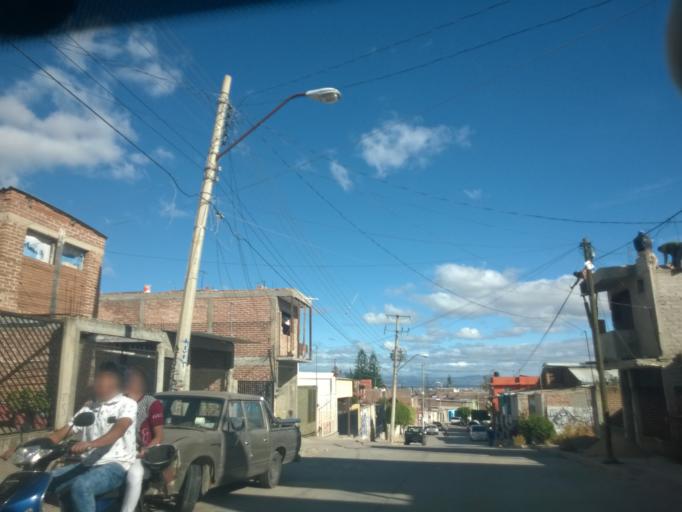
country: MX
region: Guanajuato
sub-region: Leon
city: Ejido la Joya
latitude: 21.1175
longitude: -101.7244
